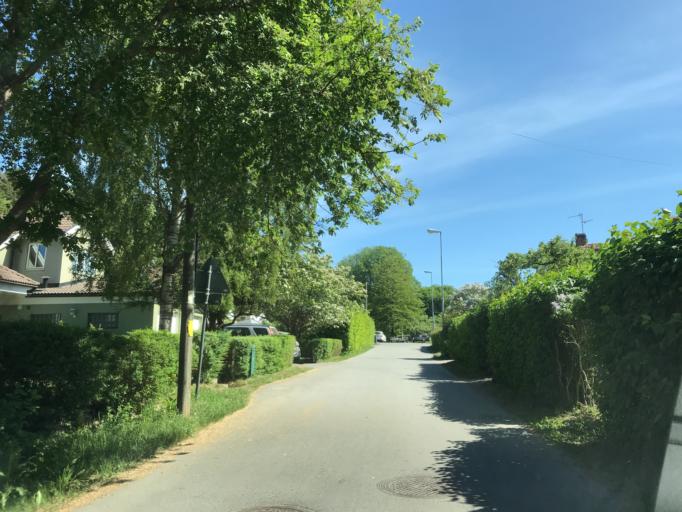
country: SE
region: Stockholm
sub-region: Sollentuna Kommun
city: Sollentuna
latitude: 59.4261
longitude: 17.9621
